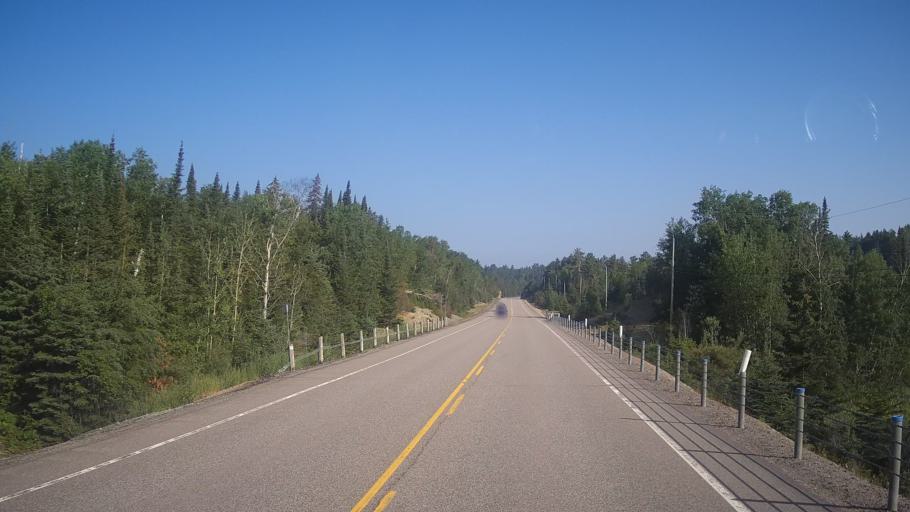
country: CA
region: Ontario
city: Rayside-Balfour
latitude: 46.7389
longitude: -81.5945
